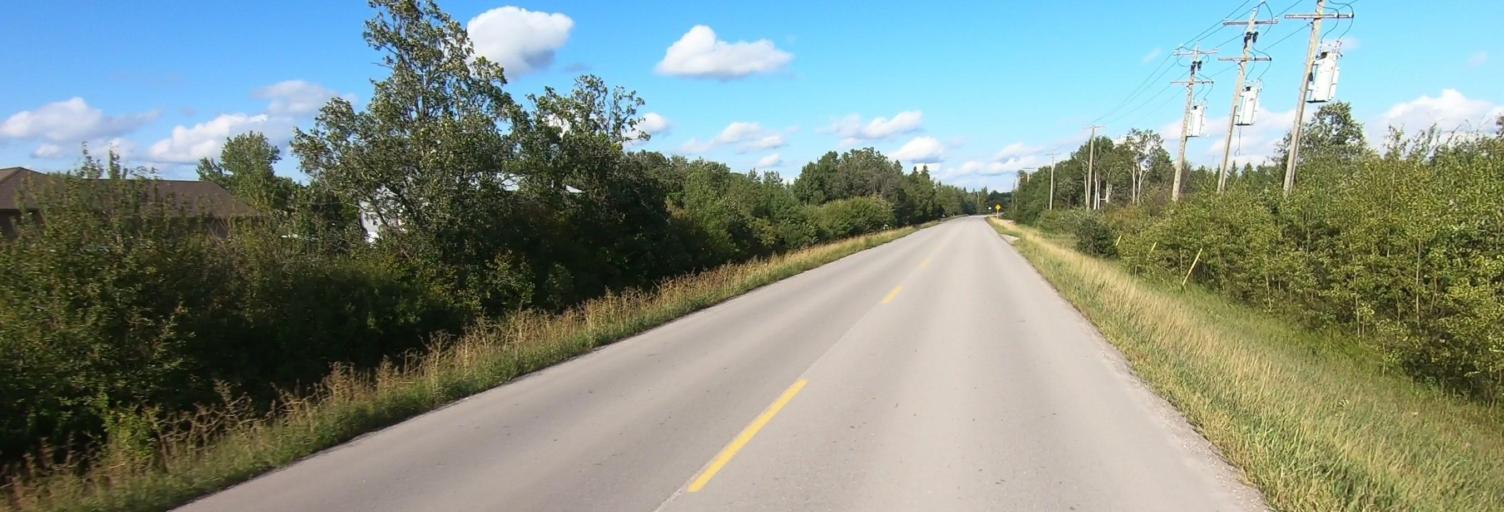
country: CA
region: Manitoba
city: Selkirk
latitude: 50.1182
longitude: -96.8855
